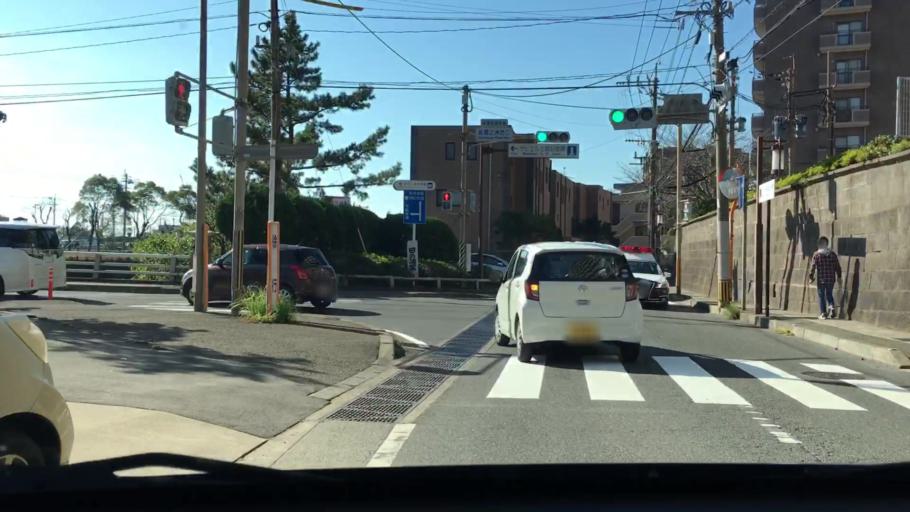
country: JP
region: Kagoshima
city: Kagoshima-shi
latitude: 31.6067
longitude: 130.5723
